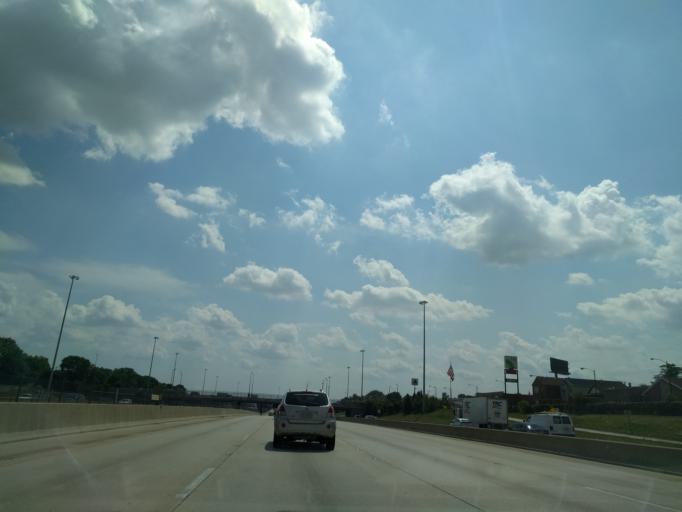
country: US
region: Illinois
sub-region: Cook County
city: Chicago
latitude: 41.8186
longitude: -87.6304
